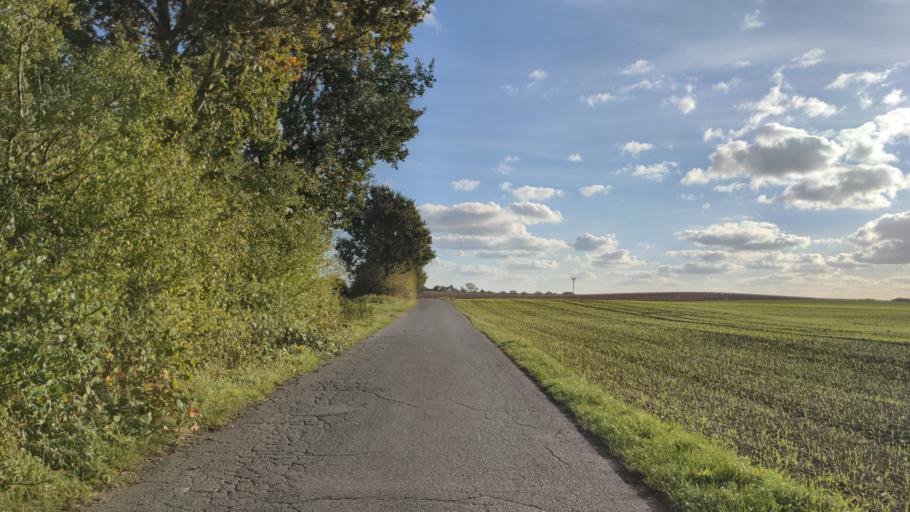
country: DE
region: Schleswig-Holstein
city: Schashagen
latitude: 54.1415
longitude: 10.9032
